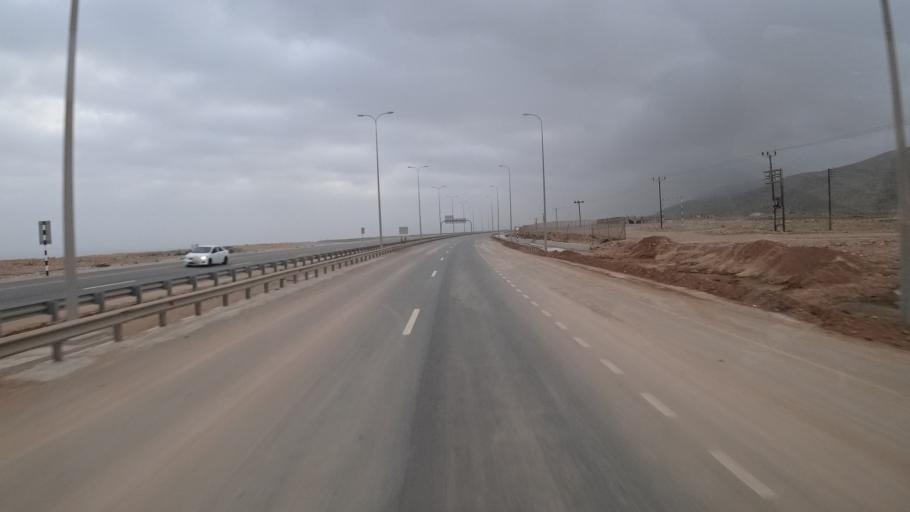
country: OM
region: Zufar
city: Salalah
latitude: 17.0307
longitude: 54.6053
